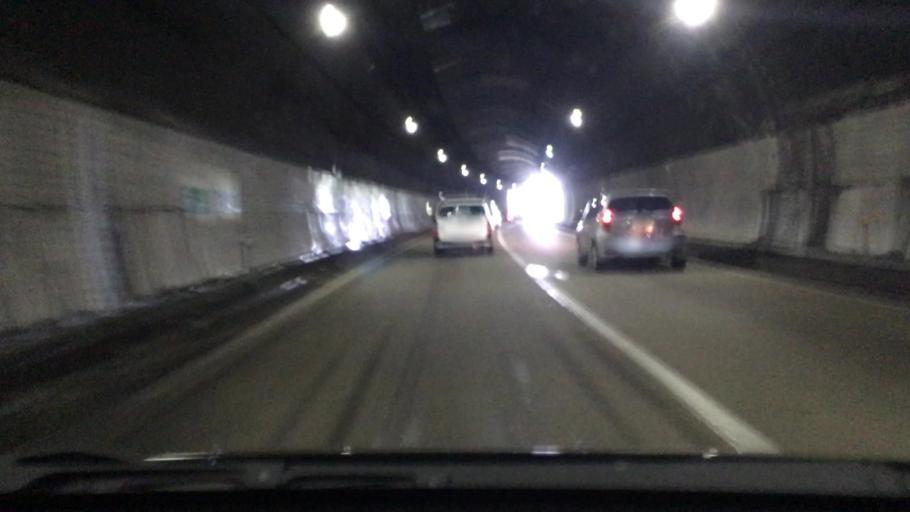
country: JP
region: Hiroshima
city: Hatsukaichi
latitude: 34.3811
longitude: 132.3909
